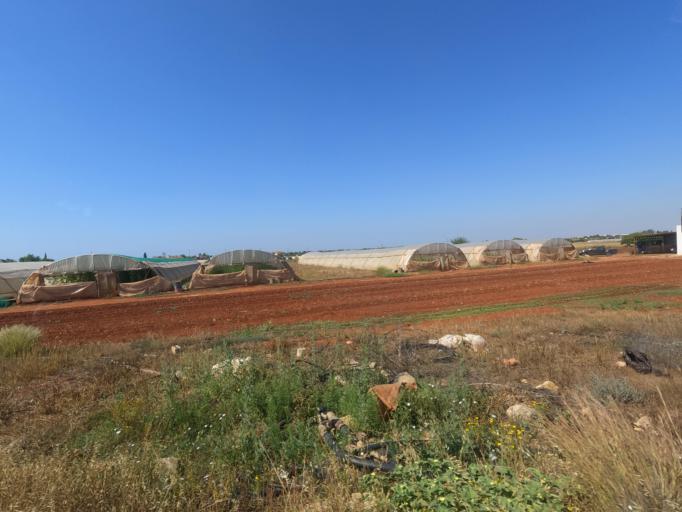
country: CY
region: Ammochostos
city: Frenaros
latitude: 35.0235
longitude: 33.9213
